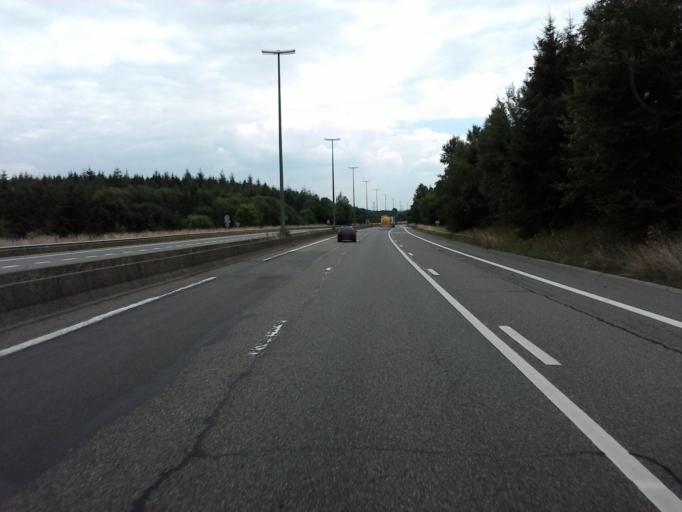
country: BE
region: Wallonia
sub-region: Province du Luxembourg
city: Houffalize
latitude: 50.1686
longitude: 5.7925
